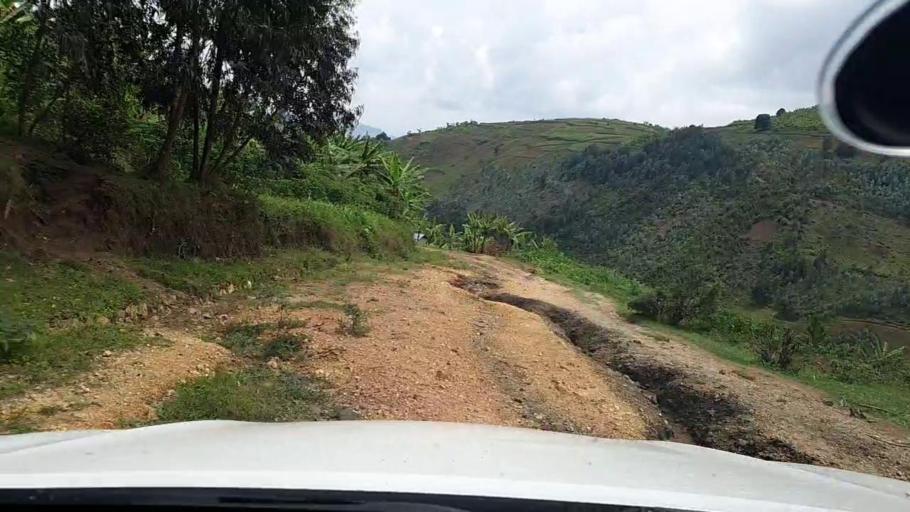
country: RW
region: Western Province
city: Kibuye
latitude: -2.1505
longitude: 29.4550
